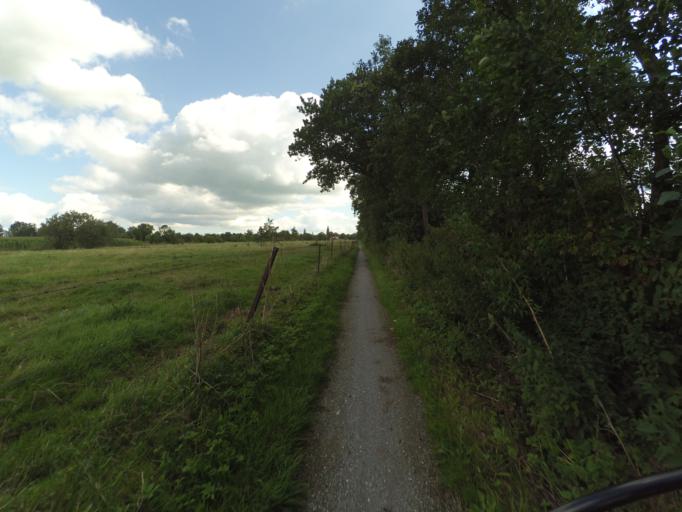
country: NL
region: Friesland
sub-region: Gemeente Achtkarspelen
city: Surhuizum
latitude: 53.2024
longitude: 6.1674
